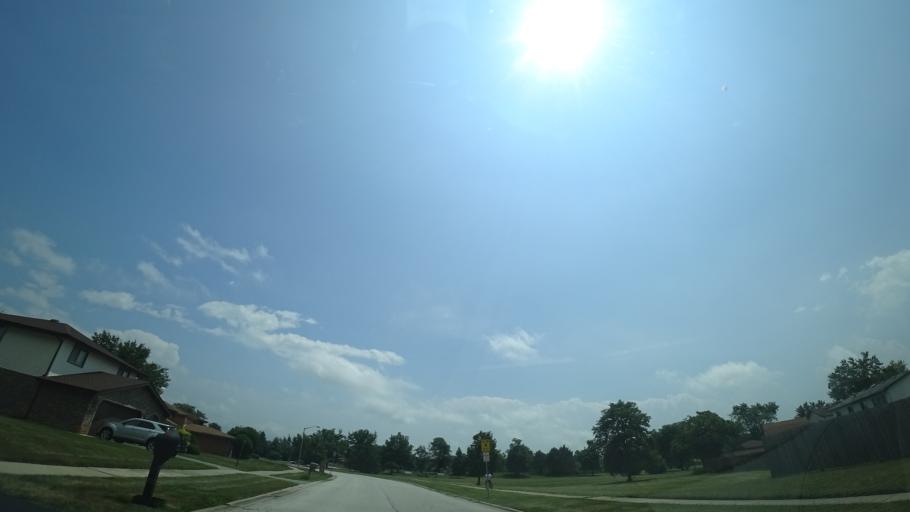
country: US
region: Illinois
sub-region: Cook County
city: Matteson
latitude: 41.5255
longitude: -87.7545
